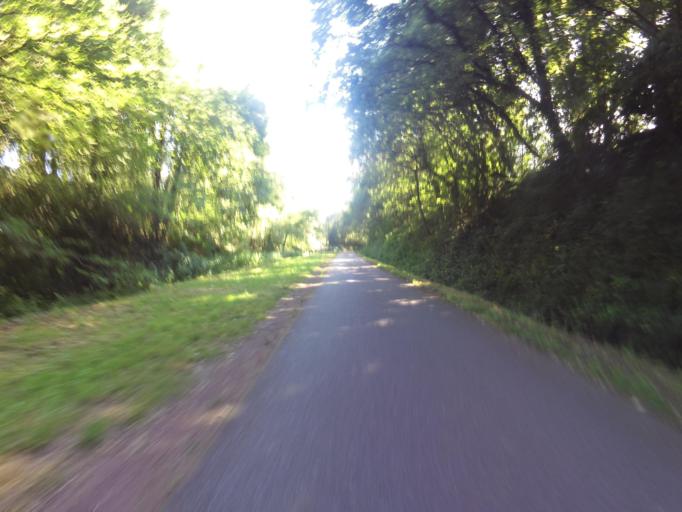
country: FR
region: Brittany
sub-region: Departement du Morbihan
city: Ploermel
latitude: 47.9274
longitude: -2.4081
